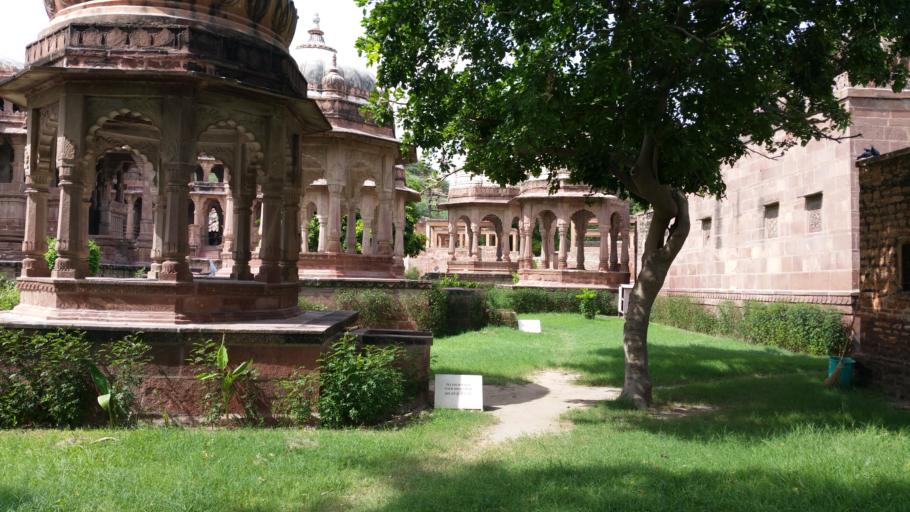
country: IN
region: Rajasthan
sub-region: Jodhpur
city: Jodhpur
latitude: 26.3521
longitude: 73.0354
